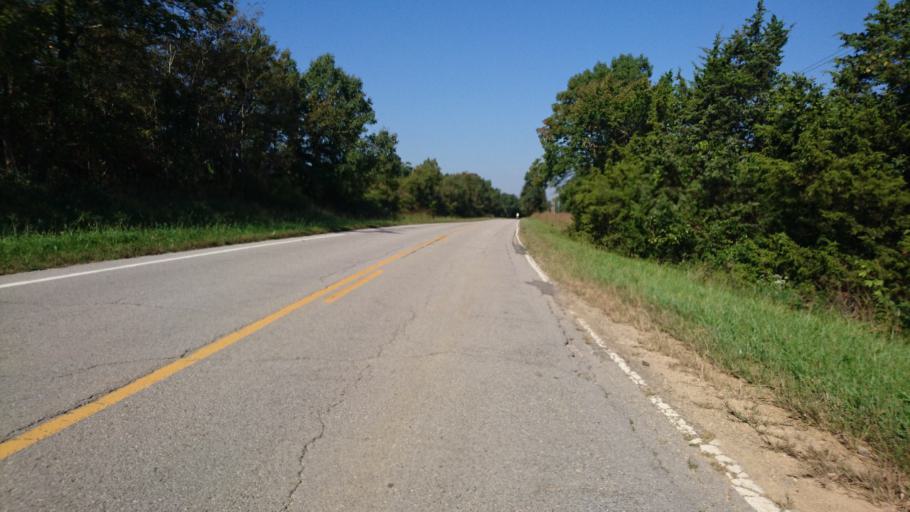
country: US
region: Missouri
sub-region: Pulaski County
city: Richland
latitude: 37.7428
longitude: -92.3504
